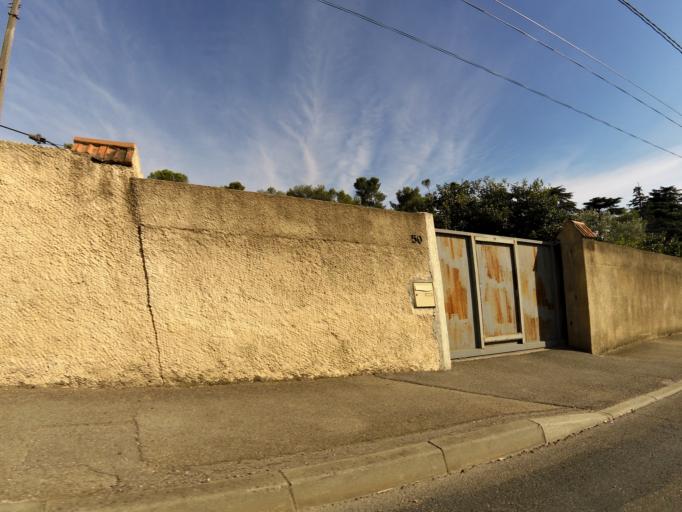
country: FR
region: Languedoc-Roussillon
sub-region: Departement du Gard
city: Nimes
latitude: 43.8440
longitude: 4.3443
